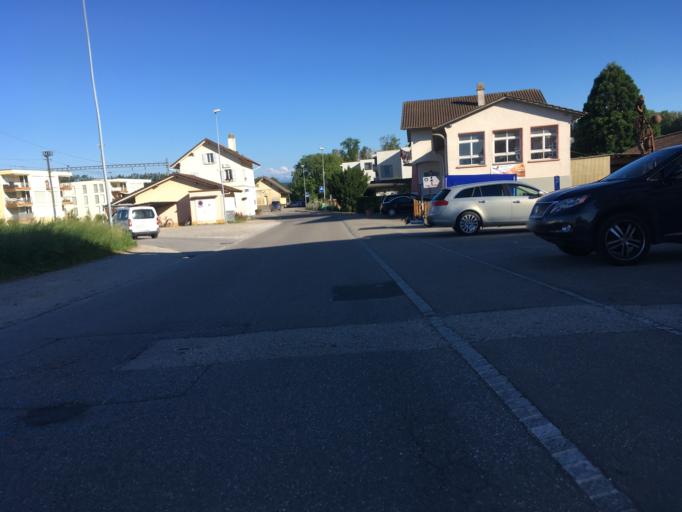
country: CH
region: Fribourg
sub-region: See District
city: Bas-Vully
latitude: 46.9647
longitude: 7.1184
